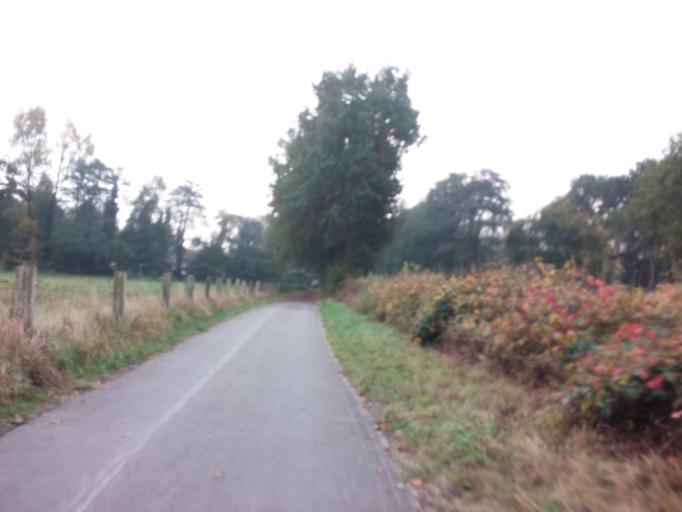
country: DE
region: North Rhine-Westphalia
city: Dorsten
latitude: 51.6372
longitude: 6.9693
